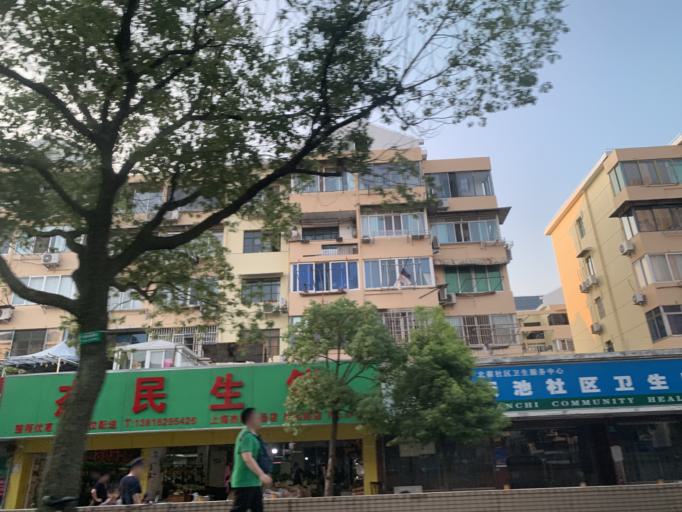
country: CN
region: Shanghai Shi
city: Huamu
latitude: 31.1871
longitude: 121.5405
